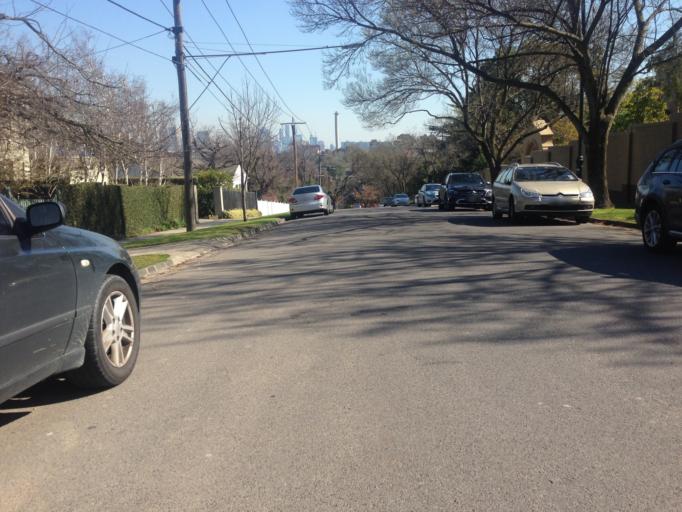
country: AU
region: Victoria
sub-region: Boroondara
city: Kew
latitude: -37.8090
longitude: 145.0167
